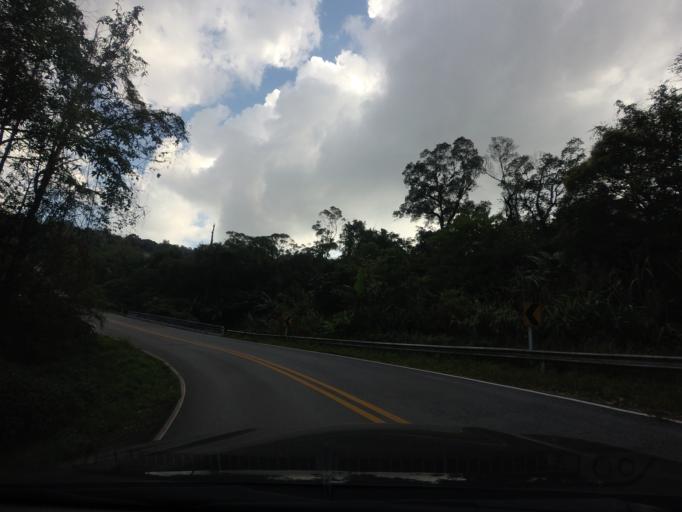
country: TH
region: Phetchabun
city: Lom Kao
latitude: 16.9422
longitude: 101.0401
